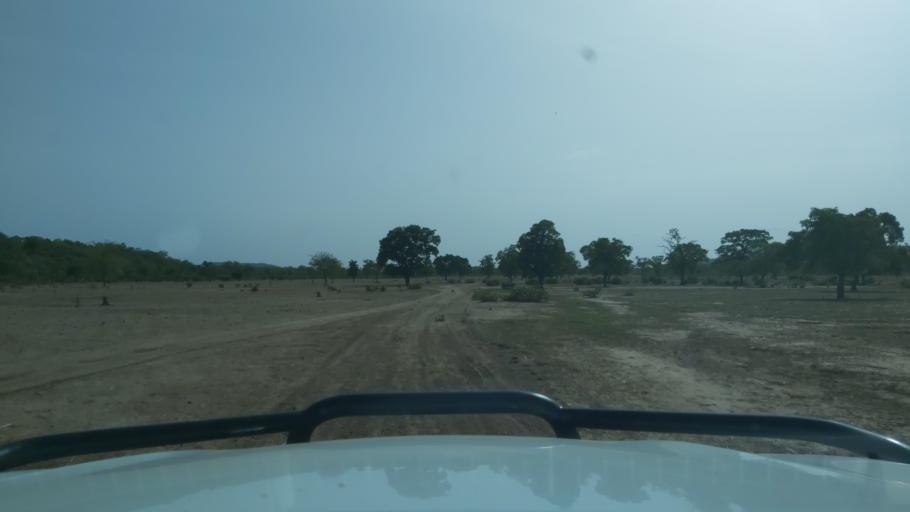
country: ML
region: Koulikoro
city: Koulikoro
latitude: 13.1754
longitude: -7.7441
